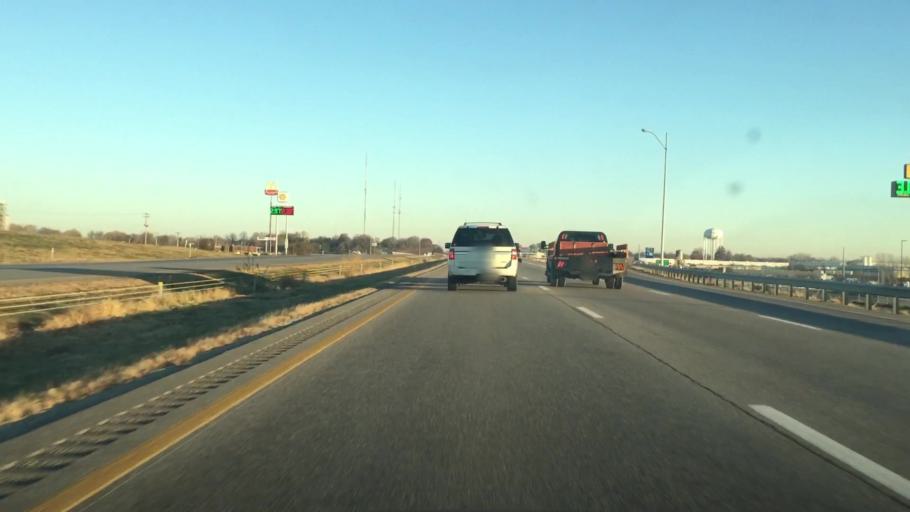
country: US
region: Missouri
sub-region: Buchanan County
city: Saint Joseph
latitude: 39.7212
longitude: -94.7886
